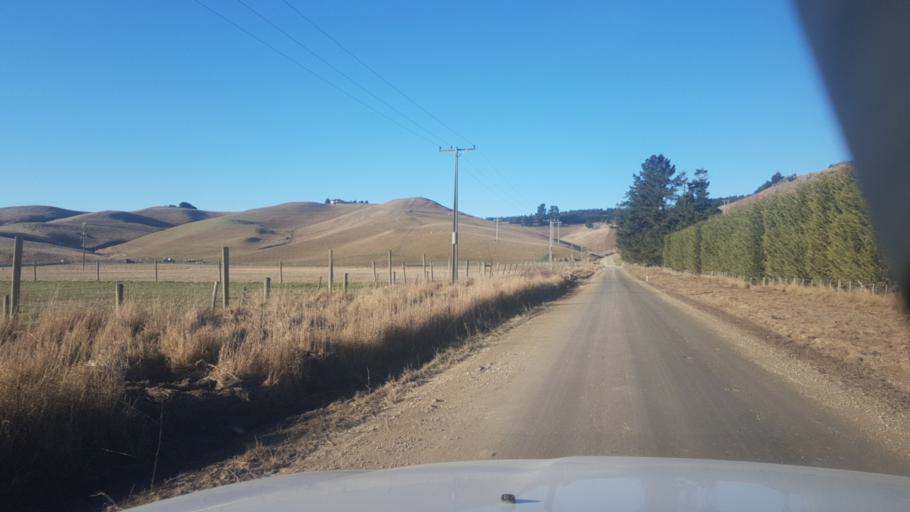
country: NZ
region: Canterbury
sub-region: Timaru District
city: Pleasant Point
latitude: -44.3435
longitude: 171.0568
